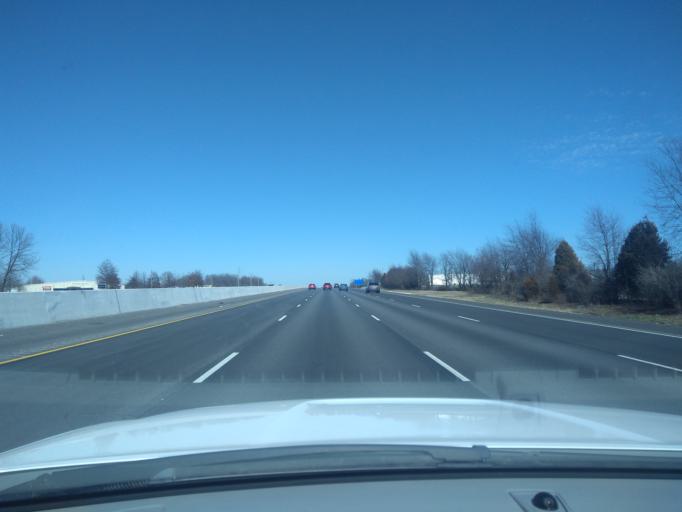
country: US
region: Arkansas
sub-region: Washington County
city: Johnson
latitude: 36.0948
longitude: -94.1890
